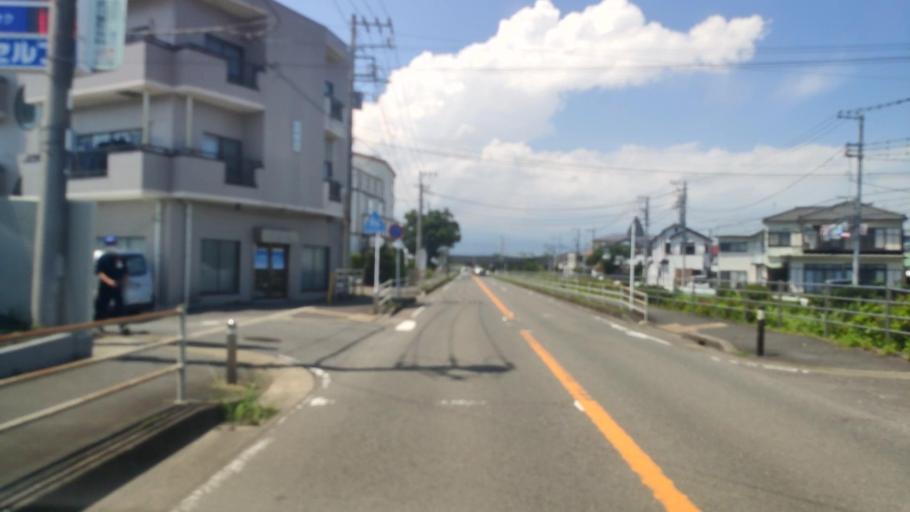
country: JP
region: Kanagawa
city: Oiso
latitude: 35.3403
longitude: 139.3086
